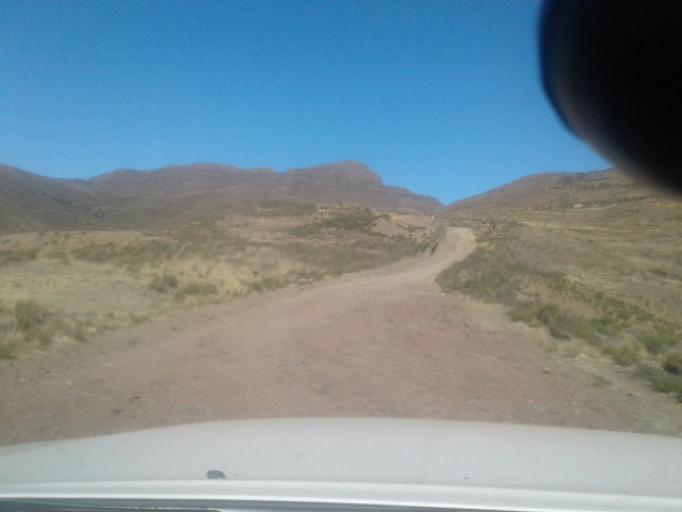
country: LS
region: Maseru
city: Nako
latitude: -29.3961
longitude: 28.0023
